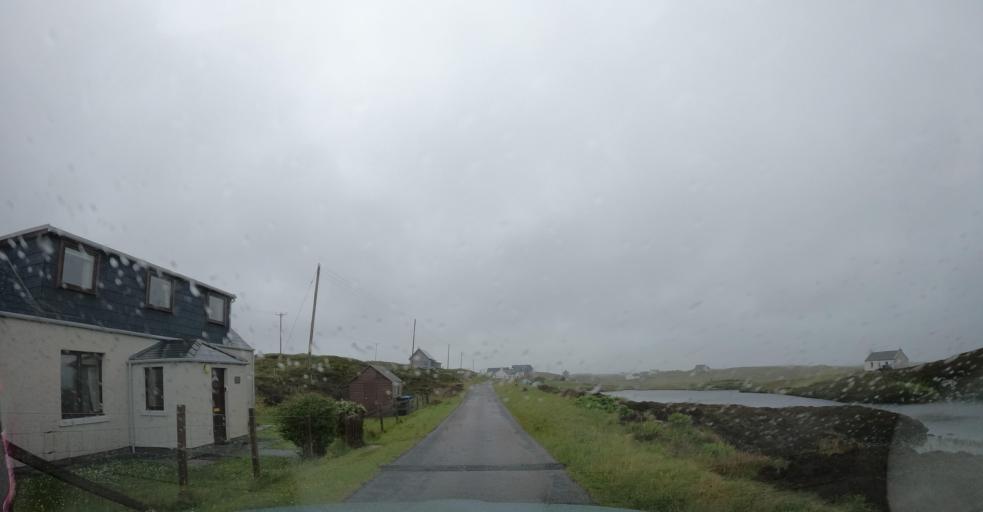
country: GB
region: Scotland
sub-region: Eilean Siar
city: Benbecula
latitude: 57.4860
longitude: -7.2176
